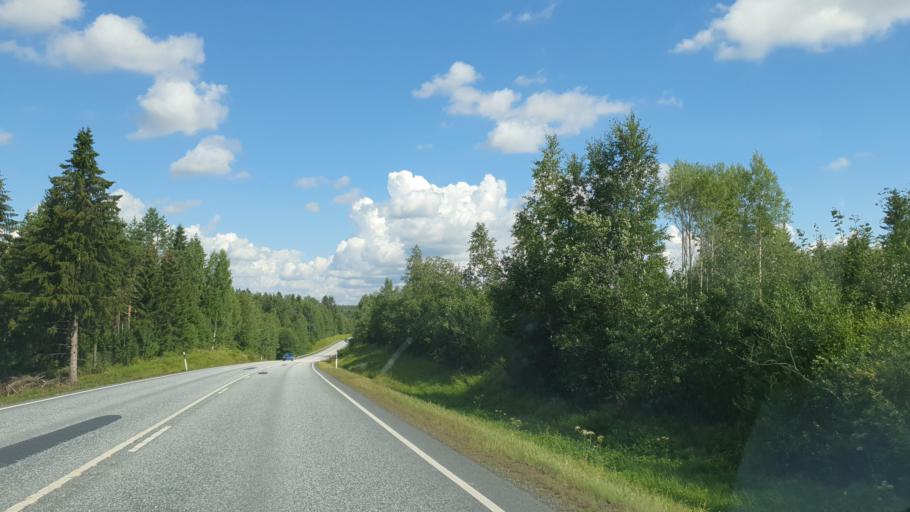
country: FI
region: Northern Savo
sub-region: Ylae-Savo
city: Sonkajaervi
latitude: 63.7544
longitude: 27.3905
